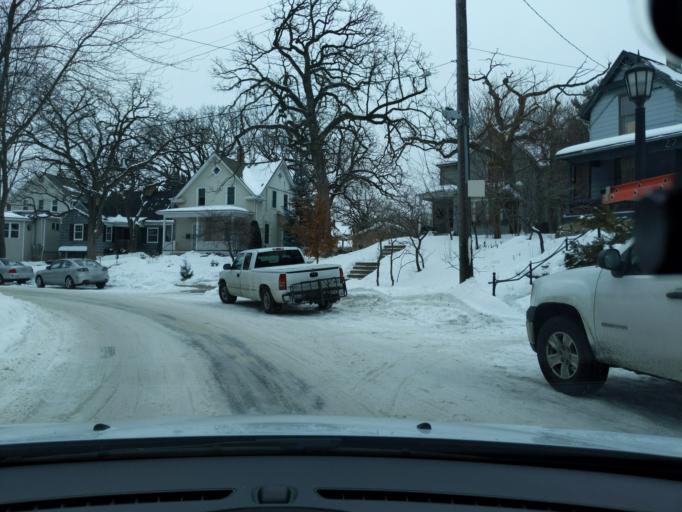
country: US
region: Minnesota
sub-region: Ramsey County
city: Lauderdale
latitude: 44.9655
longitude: -93.2102
